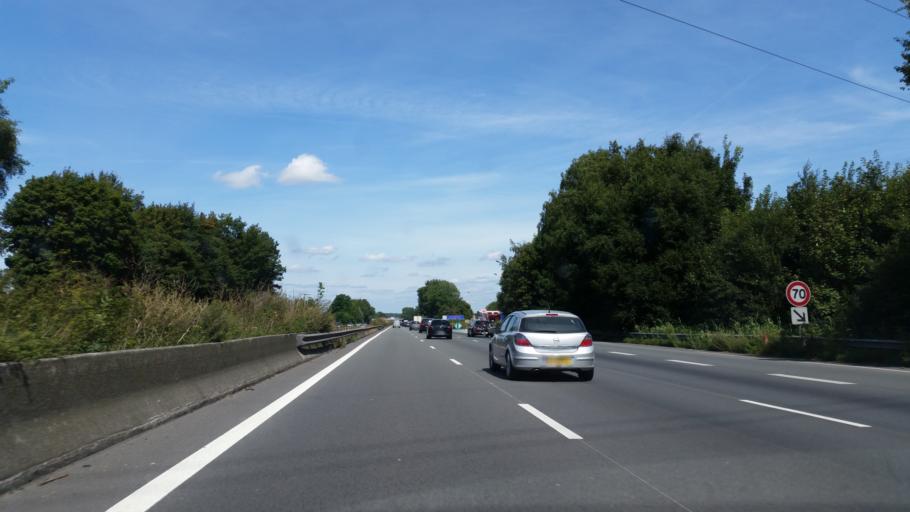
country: FR
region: Nord-Pas-de-Calais
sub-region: Departement du Nord
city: Attiches
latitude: 50.5263
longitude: 3.0431
